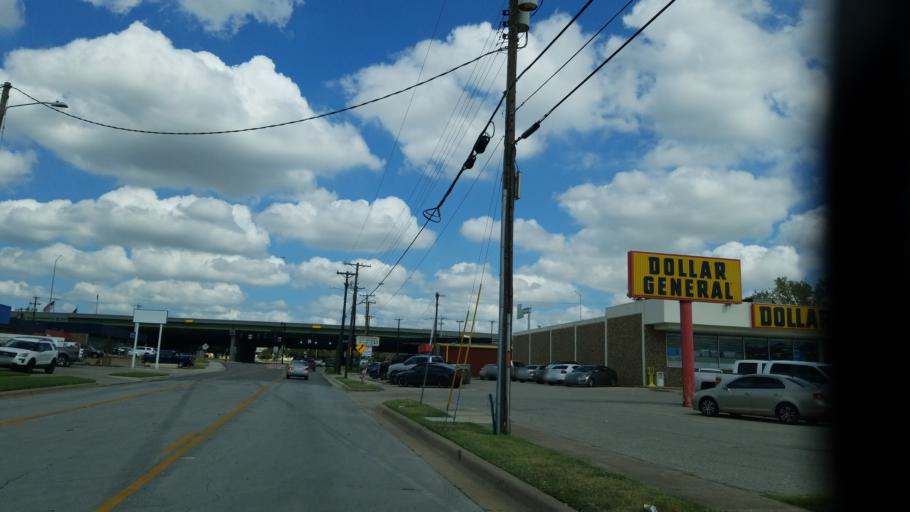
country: US
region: Texas
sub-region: Tarrant County
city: Euless
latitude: 32.8355
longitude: -97.0907
